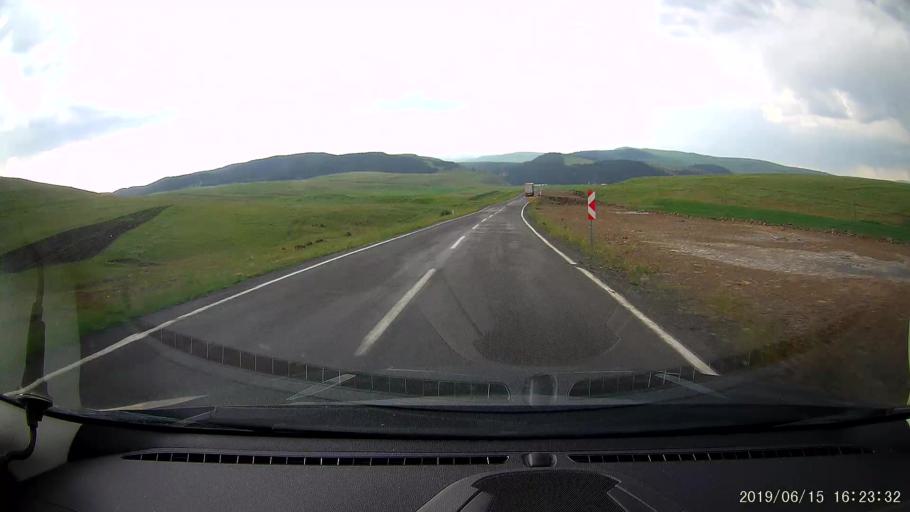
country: TR
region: Ardahan
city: Hanak
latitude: 41.1771
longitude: 42.8634
